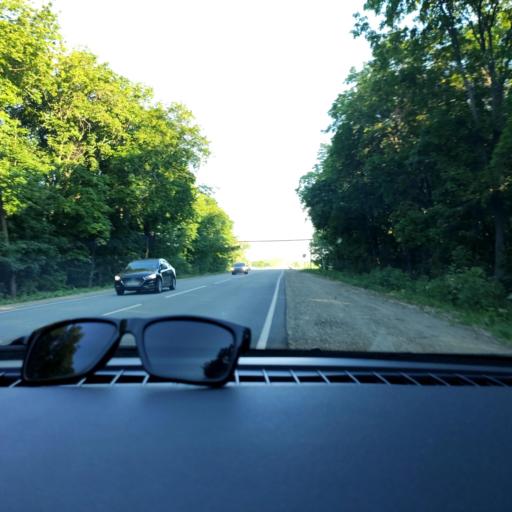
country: RU
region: Samara
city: Dubovyy Umet
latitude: 53.0283
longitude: 50.4667
